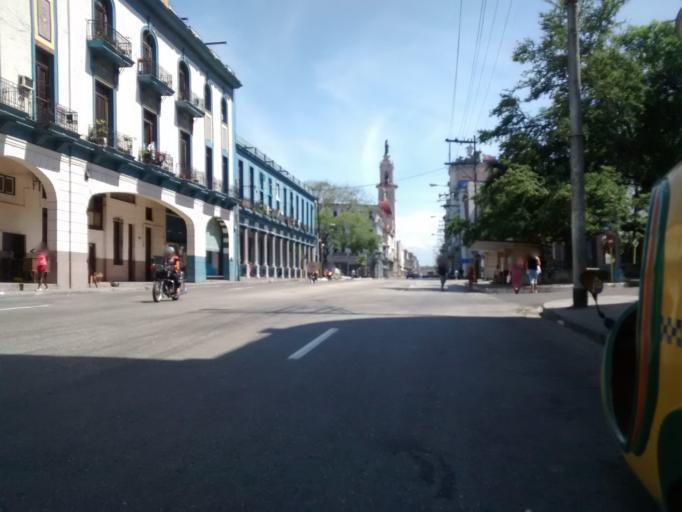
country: CU
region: La Habana
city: Havana
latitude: 23.1397
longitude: -82.3785
